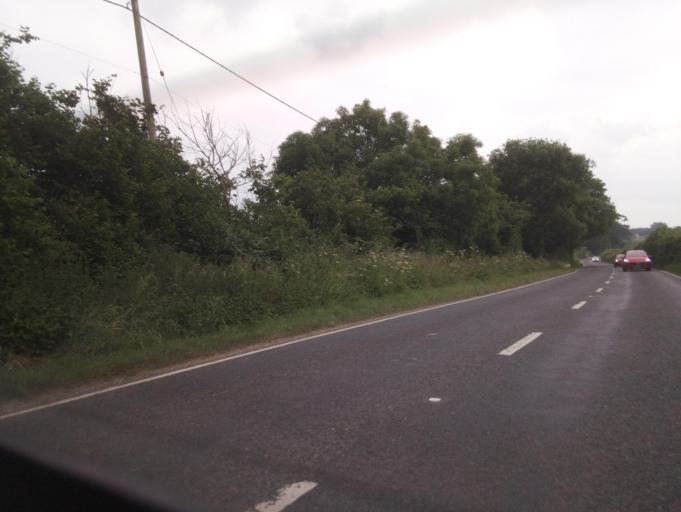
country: GB
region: England
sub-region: Somerset
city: Yeovil
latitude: 50.9679
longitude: -2.6158
